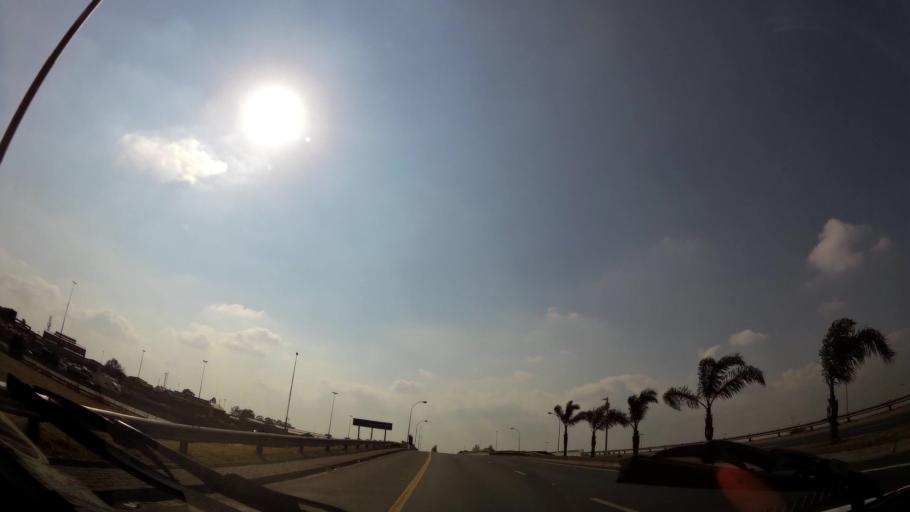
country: ZA
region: Gauteng
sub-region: Ekurhuleni Metropolitan Municipality
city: Germiston
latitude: -26.1764
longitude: 28.1973
